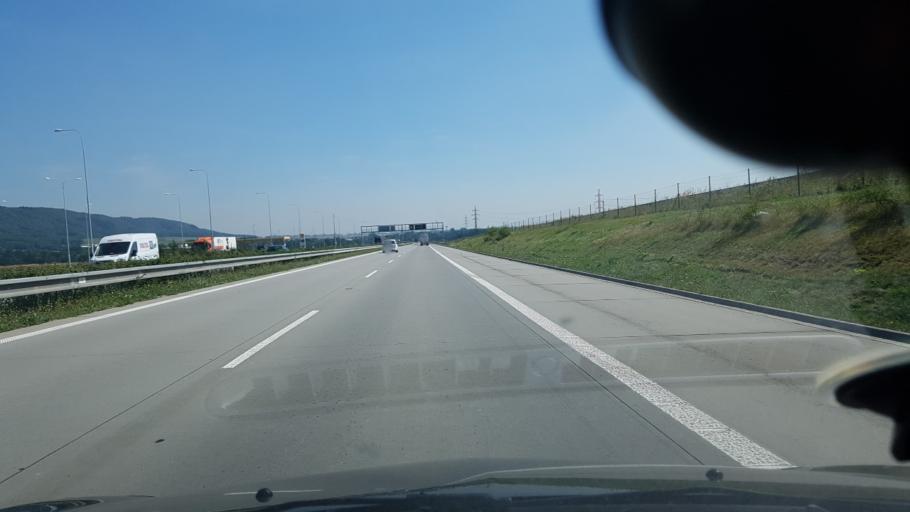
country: CZ
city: Odry
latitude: 49.6306
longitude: 17.8406
